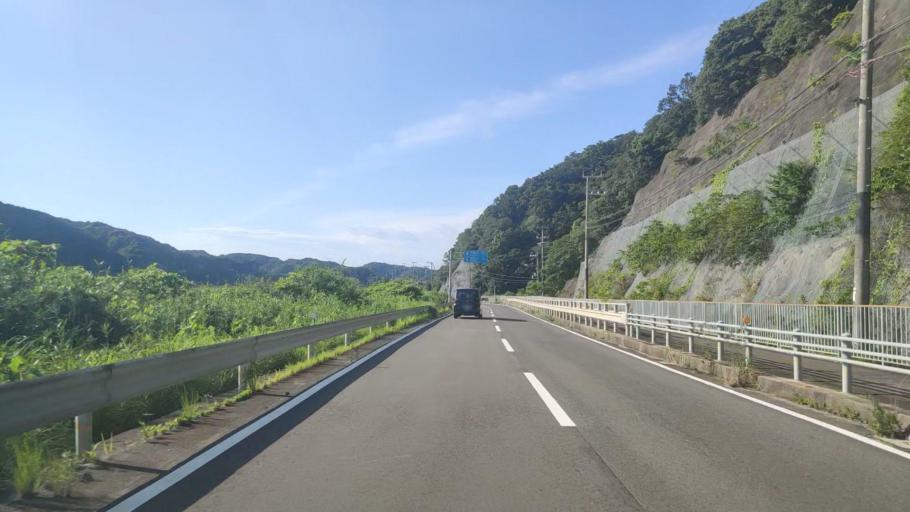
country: JP
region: Wakayama
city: Tanabe
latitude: 33.6562
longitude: 135.4016
